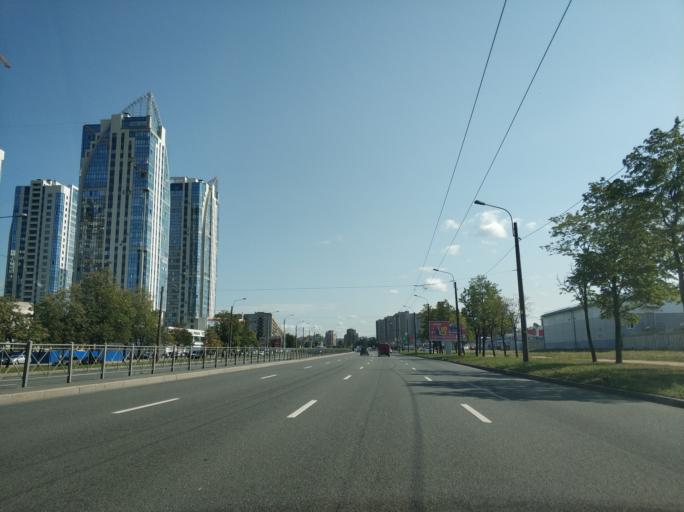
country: RU
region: St.-Petersburg
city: Kupchino
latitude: 59.8524
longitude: 30.3456
